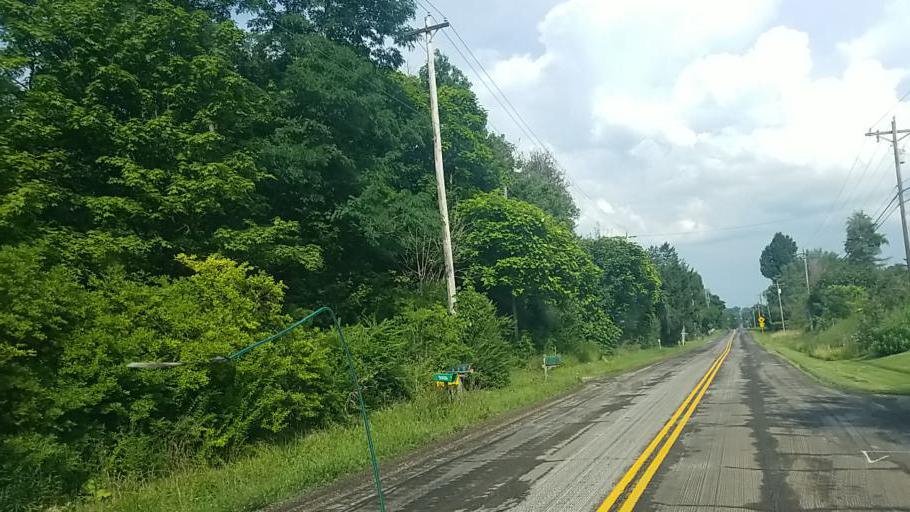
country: US
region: Ohio
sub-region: Medina County
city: Westfield Center
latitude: 41.0273
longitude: -81.9700
